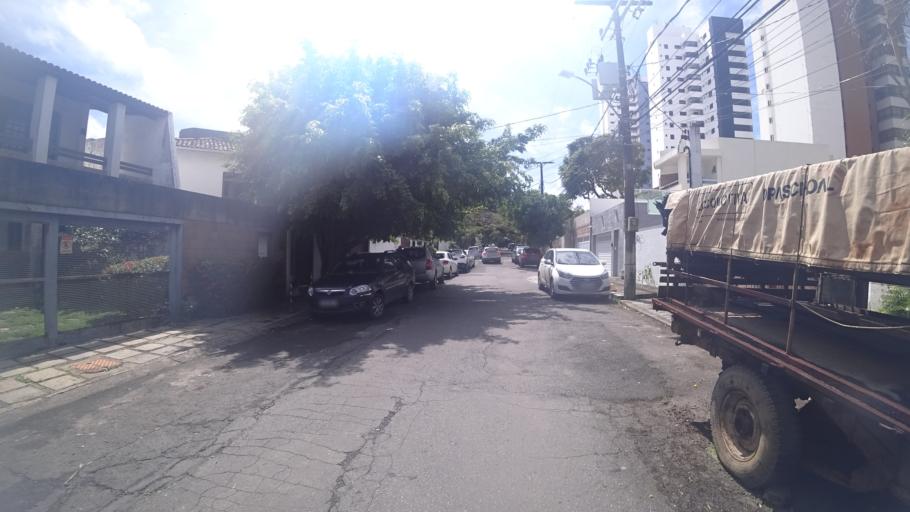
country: BR
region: Bahia
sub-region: Salvador
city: Salvador
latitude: -12.9929
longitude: -38.4574
